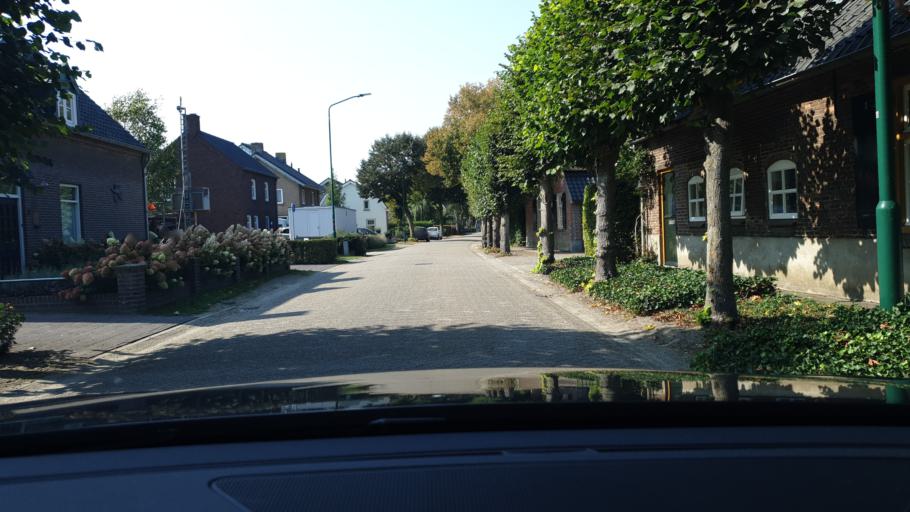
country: NL
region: North Brabant
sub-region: Gemeente Bernheze
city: Loosbroek
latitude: 51.6558
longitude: 5.4680
